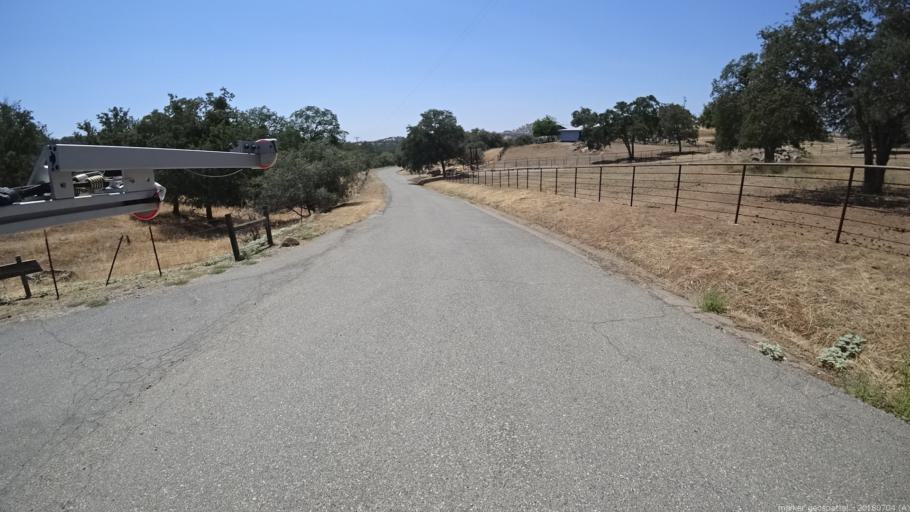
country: US
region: California
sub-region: Madera County
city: Yosemite Lakes
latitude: 37.1377
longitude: -119.6780
